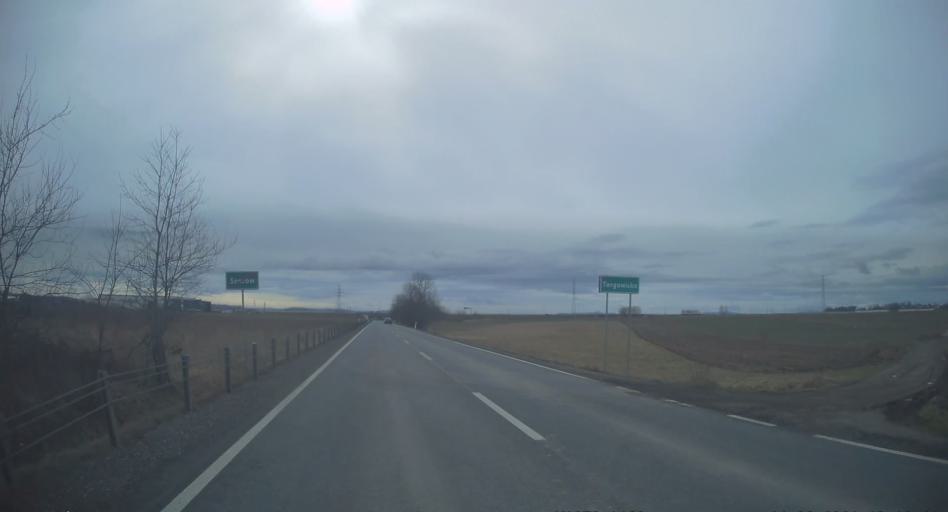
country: PL
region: Lesser Poland Voivodeship
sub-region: Powiat wielicki
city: Szarow
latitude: 49.9952
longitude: 20.2780
